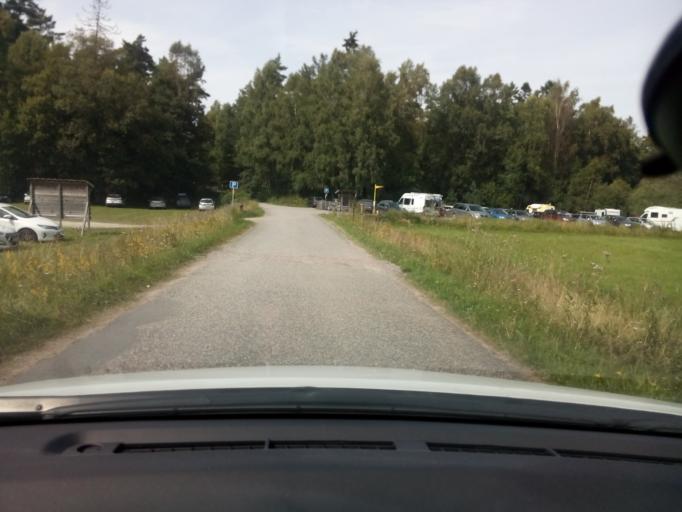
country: SE
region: Soedermanland
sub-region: Trosa Kommun
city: Trosa
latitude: 58.7478
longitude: 17.3817
